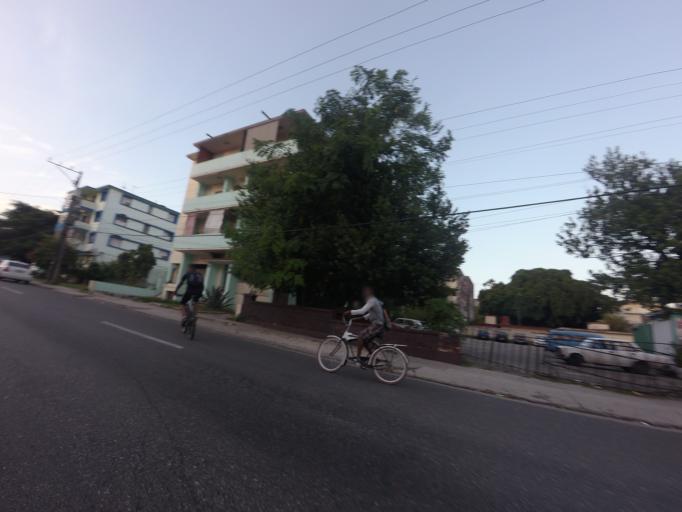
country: CU
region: La Habana
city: Havana
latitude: 23.1176
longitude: -82.4012
